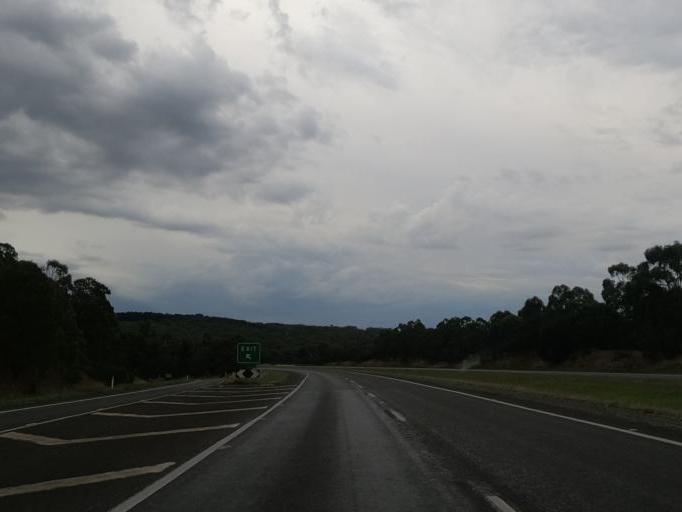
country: AU
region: Victoria
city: Brown Hill
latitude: -37.5525
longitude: 143.9101
